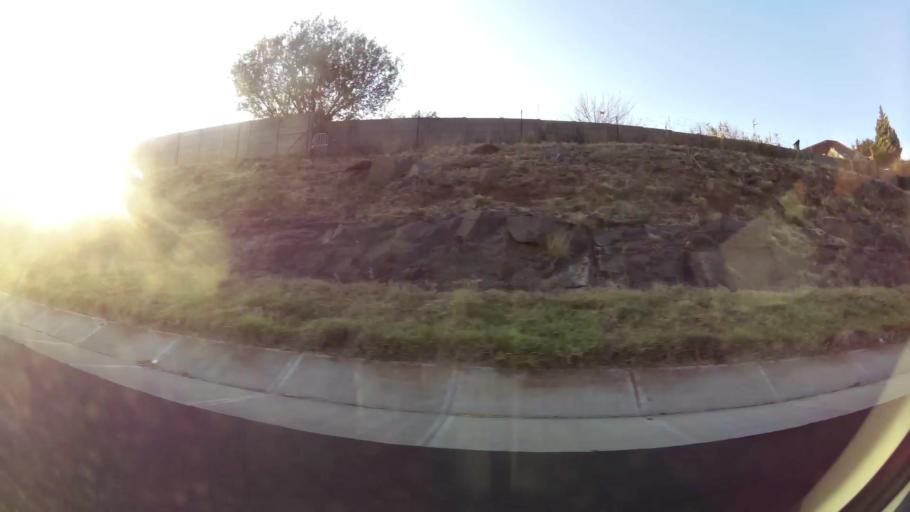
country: ZA
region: Orange Free State
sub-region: Mangaung Metropolitan Municipality
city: Bloemfontein
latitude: -29.0974
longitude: 26.1665
